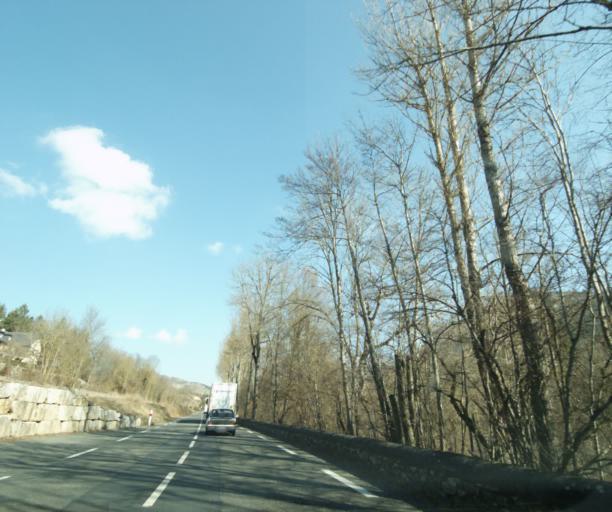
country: FR
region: Languedoc-Roussillon
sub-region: Departement de la Lozere
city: Chanac
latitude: 44.4888
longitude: 3.3890
